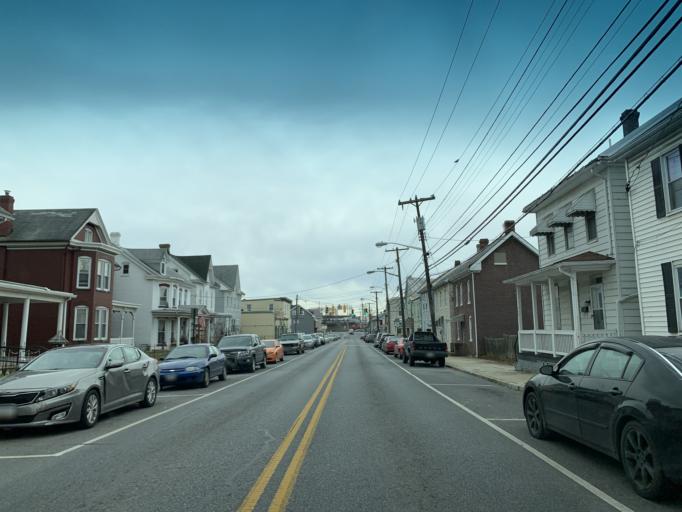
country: US
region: Maryland
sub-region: Washington County
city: Hagerstown
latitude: 39.6497
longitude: -77.7266
